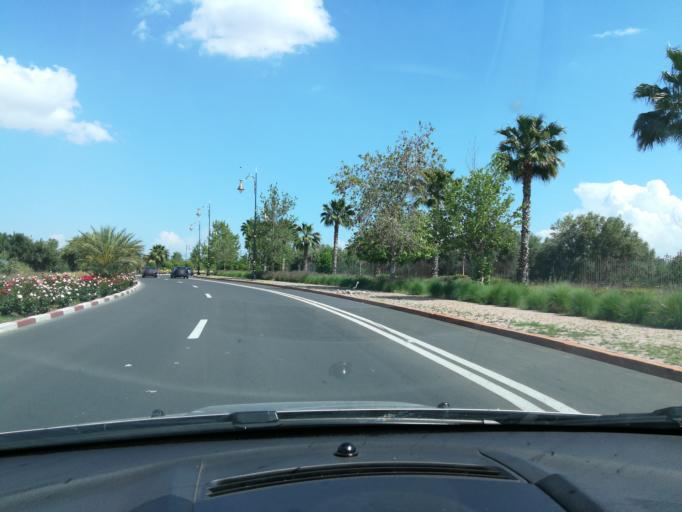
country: MA
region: Marrakech-Tensift-Al Haouz
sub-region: Marrakech
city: Marrakesh
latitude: 31.6126
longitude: -8.0061
